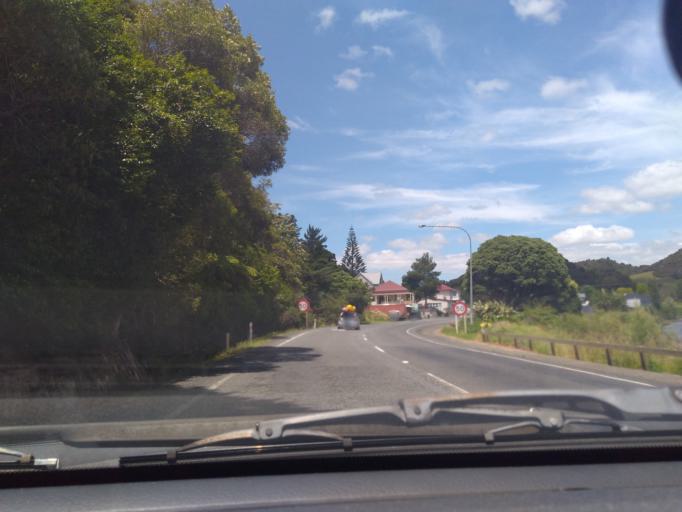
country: NZ
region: Northland
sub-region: Far North District
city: Kerikeri
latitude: -35.0990
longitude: 173.7770
